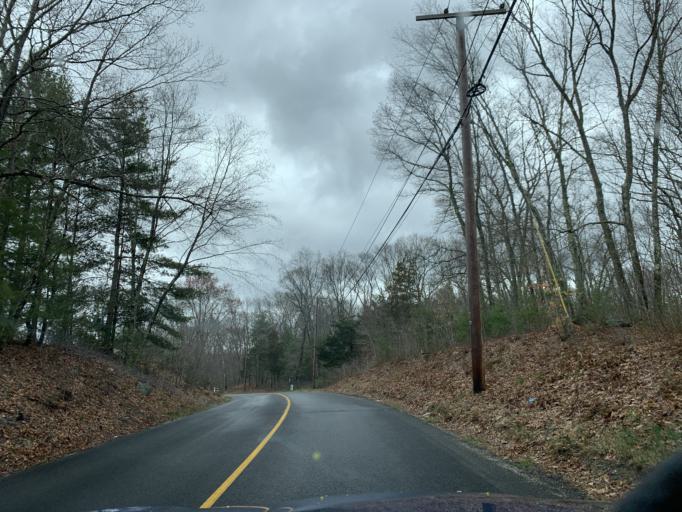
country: US
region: Massachusetts
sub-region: Bristol County
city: Rehoboth
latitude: 41.8892
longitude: -71.2096
